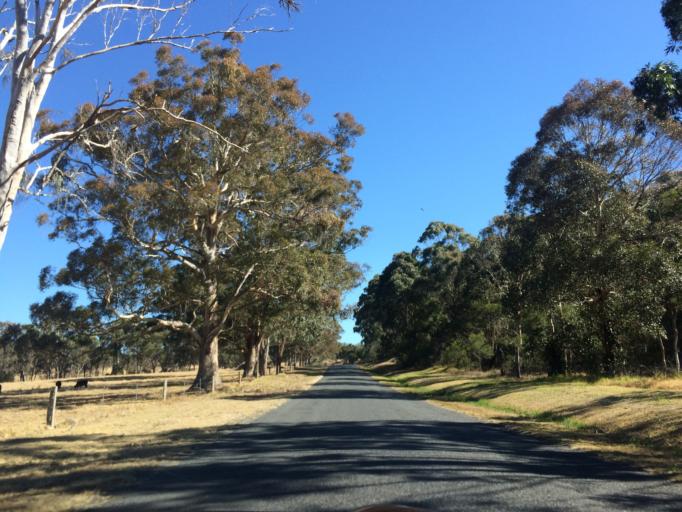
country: AU
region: Queensland
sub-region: Southern Downs
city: Stanthorpe
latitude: -28.6522
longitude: 152.0831
